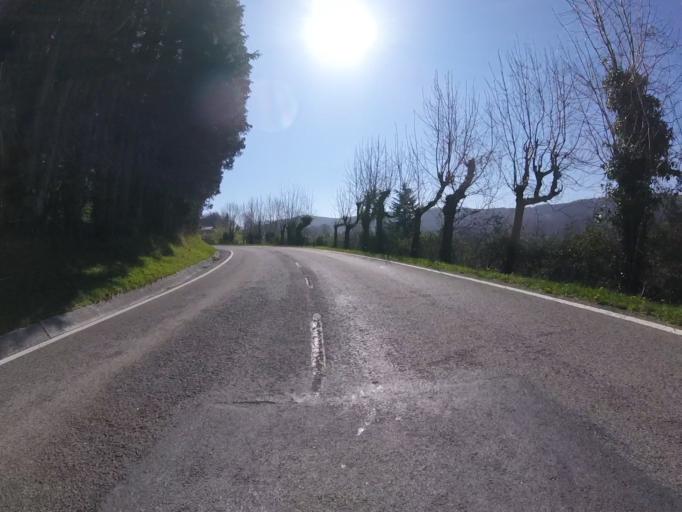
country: ES
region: Navarre
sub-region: Provincia de Navarra
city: Leitza
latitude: 43.0884
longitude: -1.8884
